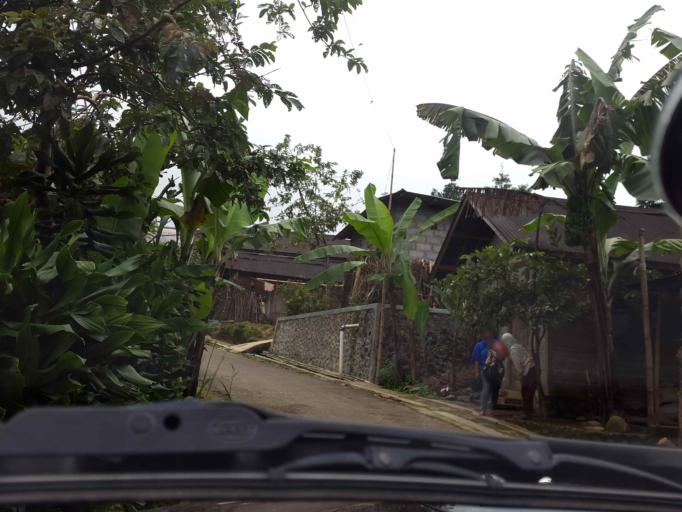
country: ID
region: Central Java
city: Wonosobo
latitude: -7.2616
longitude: 109.8503
